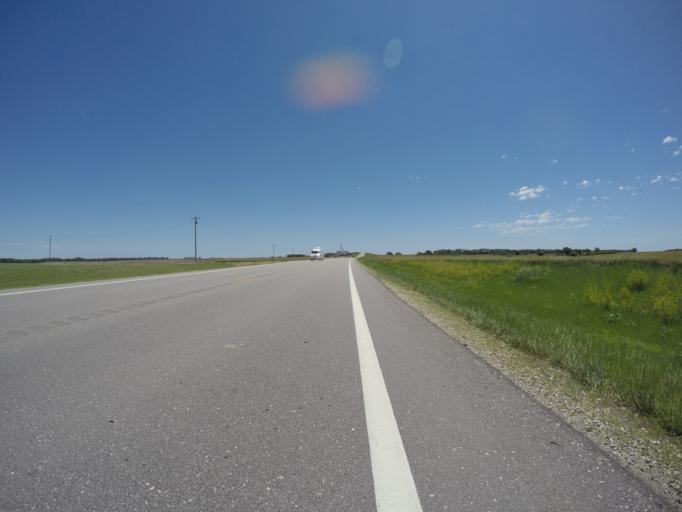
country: US
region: Kansas
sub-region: Republic County
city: Belleville
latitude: 39.8130
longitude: -97.7242
